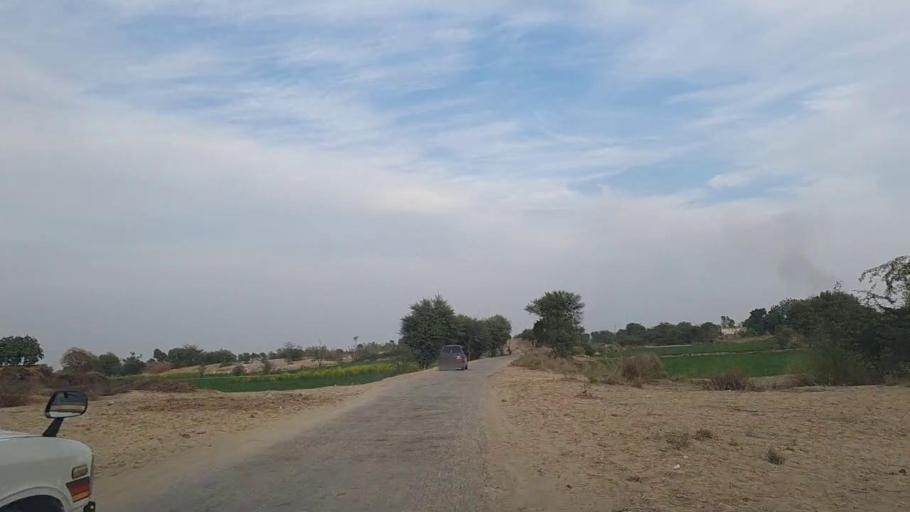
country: PK
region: Sindh
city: Daur
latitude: 26.5282
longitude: 68.4168
